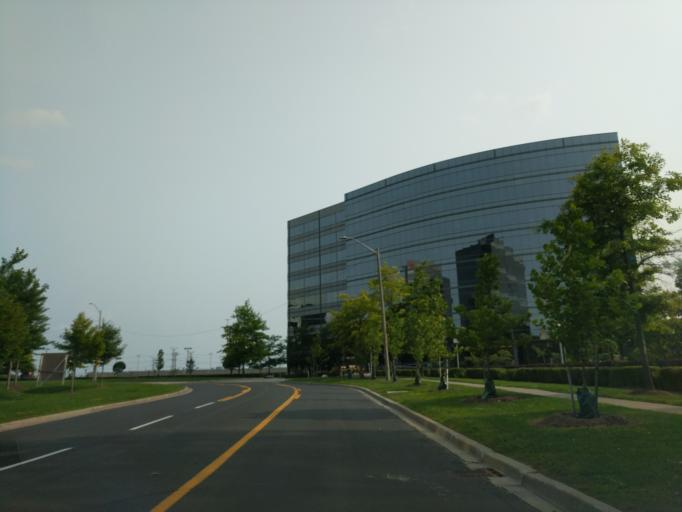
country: CA
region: Ontario
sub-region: York
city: Richmond Hill
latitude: 43.8398
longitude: -79.3833
